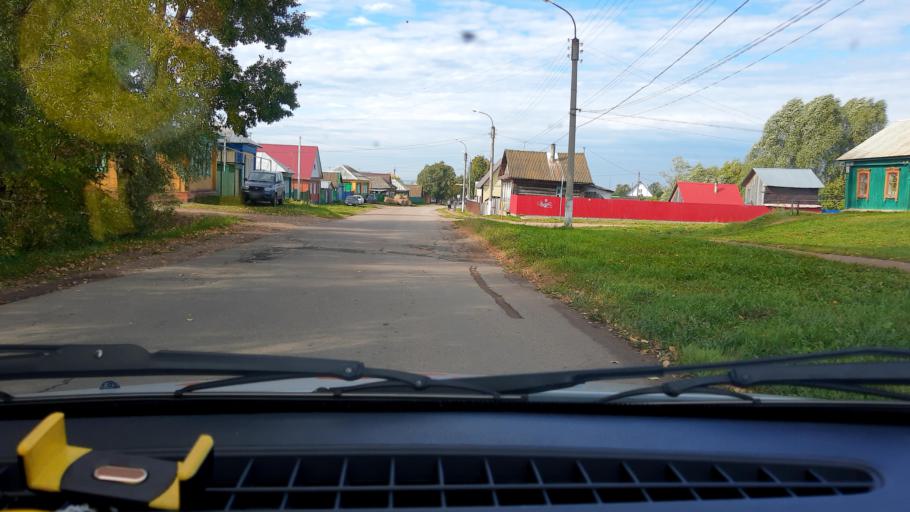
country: RU
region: Bashkortostan
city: Blagoveshchensk
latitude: 55.0275
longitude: 55.9929
